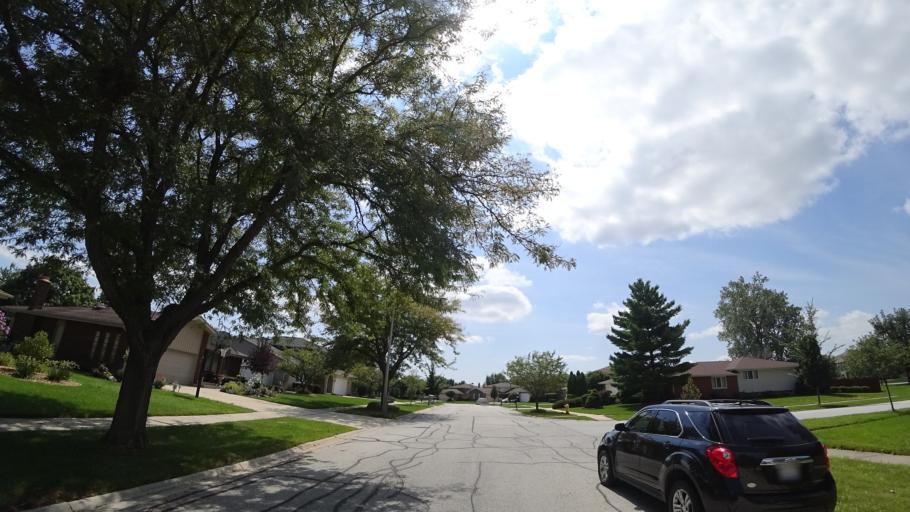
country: US
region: Illinois
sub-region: Cook County
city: Orland Hills
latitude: 41.5703
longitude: -87.8413
